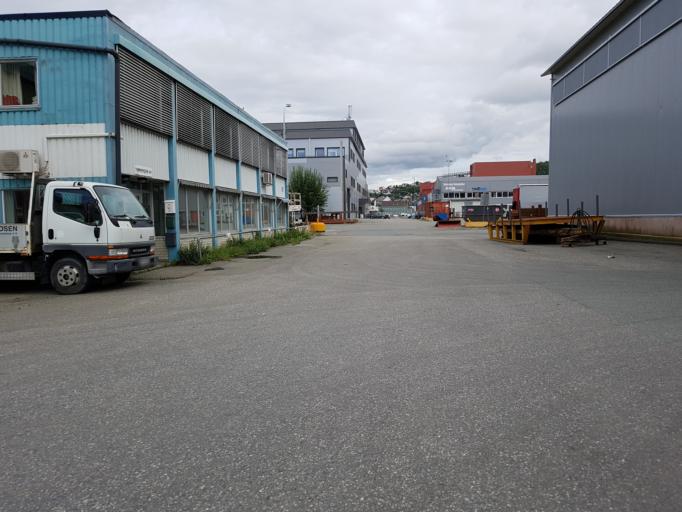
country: NO
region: Sor-Trondelag
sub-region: Trondheim
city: Trondheim
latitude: 63.4392
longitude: 10.4134
